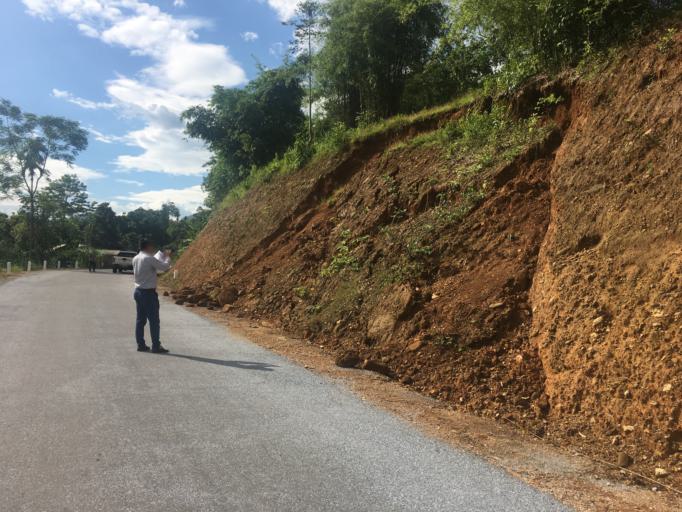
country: VN
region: Ha Giang
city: Thanh Pho Ha Giang
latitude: 22.8752
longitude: 105.0483
